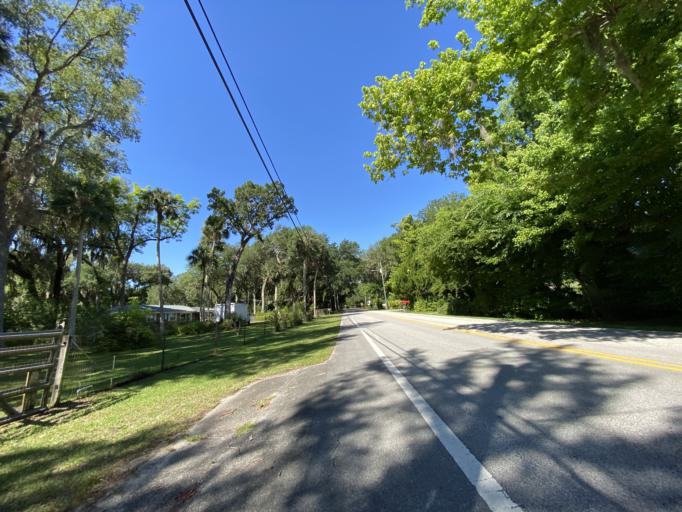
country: US
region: Florida
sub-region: Volusia County
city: Port Orange
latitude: 29.1403
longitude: -81.0060
